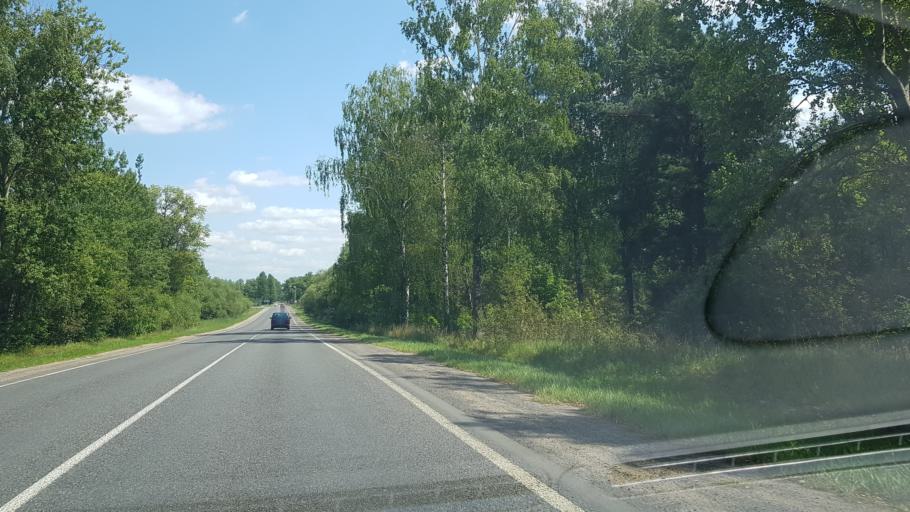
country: BY
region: Mogilev
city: Babruysk
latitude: 53.1074
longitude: 29.1855
